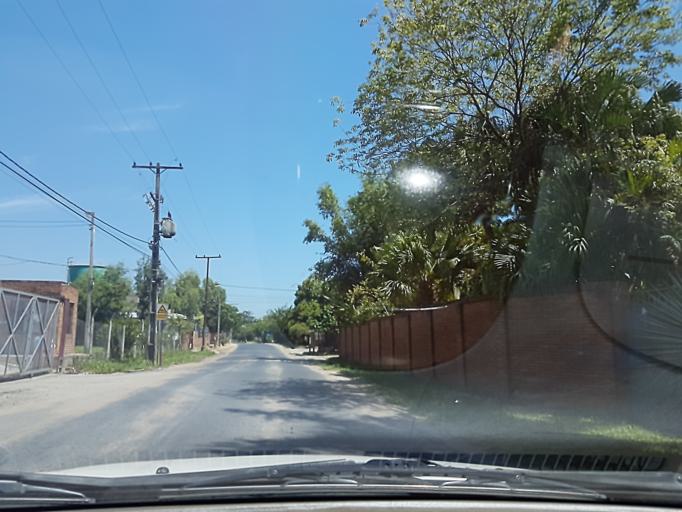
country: PY
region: Central
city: Fernando de la Mora
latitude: -25.2701
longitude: -57.5193
